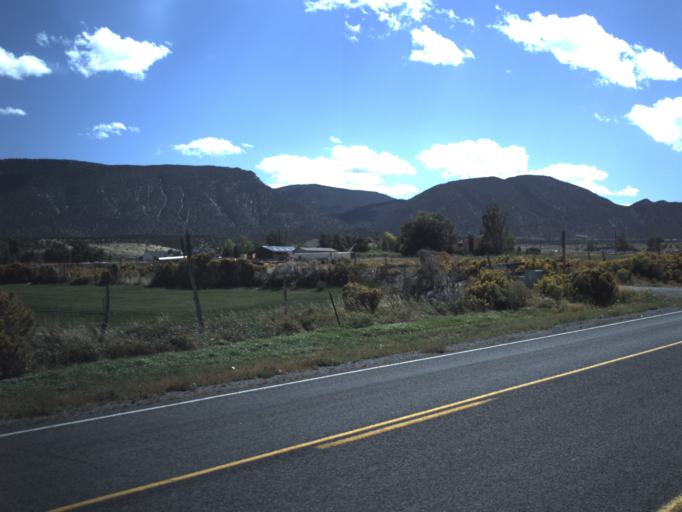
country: US
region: Utah
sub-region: Iron County
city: Enoch
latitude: 37.7435
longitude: -113.0553
